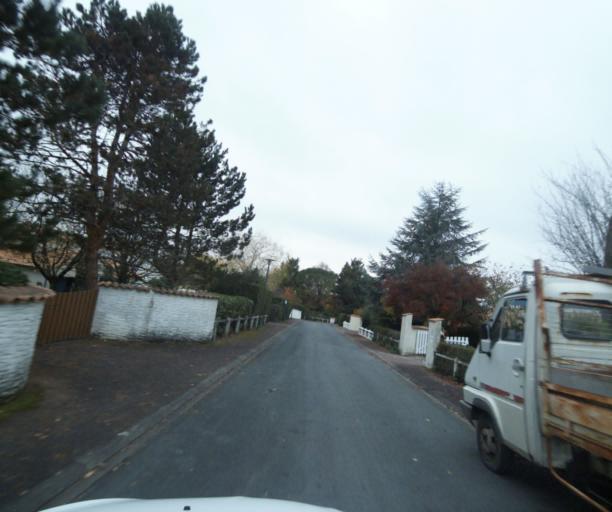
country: FR
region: Poitou-Charentes
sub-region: Departement de la Charente-Maritime
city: Fontcouverte
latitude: 45.7422
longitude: -0.5964
